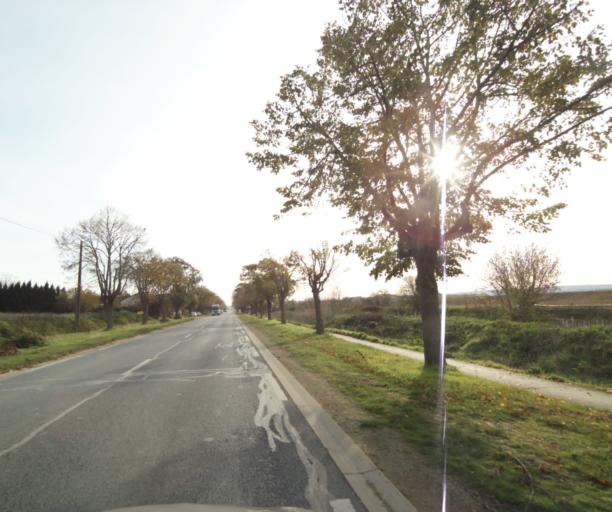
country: FR
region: Ile-de-France
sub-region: Departement des Yvelines
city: Triel-sur-Seine
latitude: 48.9608
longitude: 2.0162
